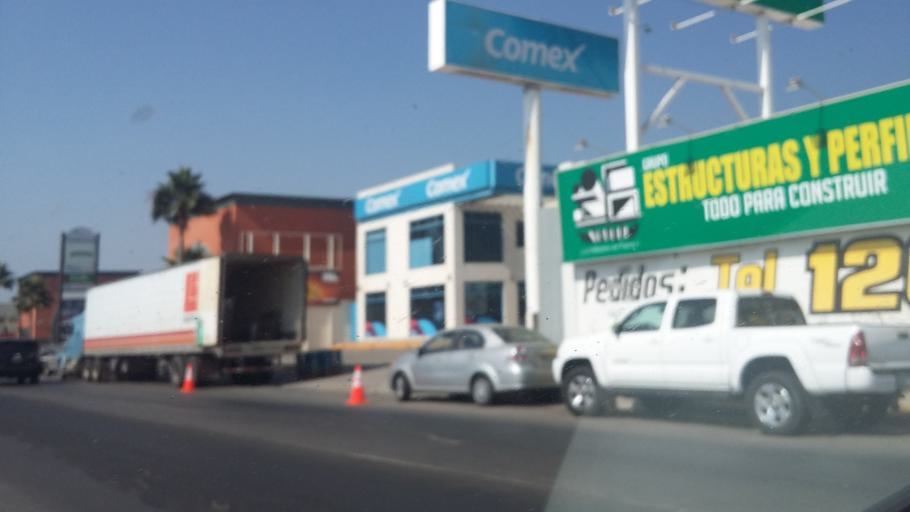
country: MX
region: Baja California
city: Ensenada
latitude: 31.7939
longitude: -116.5934
